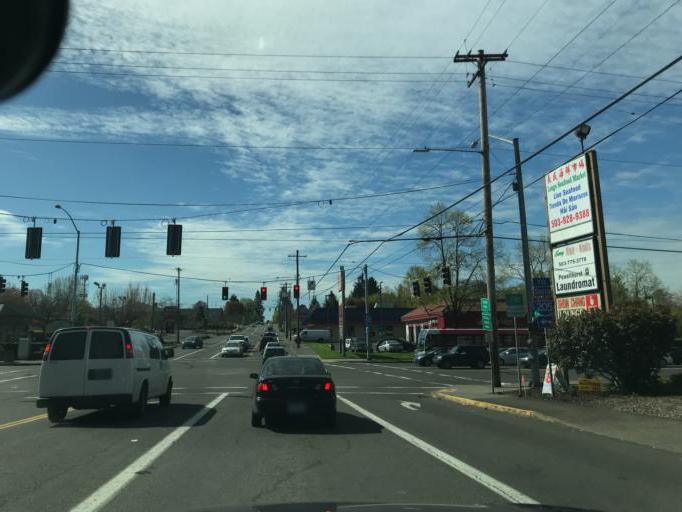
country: US
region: Oregon
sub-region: Multnomah County
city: Lents
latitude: 45.4978
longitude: -122.5686
